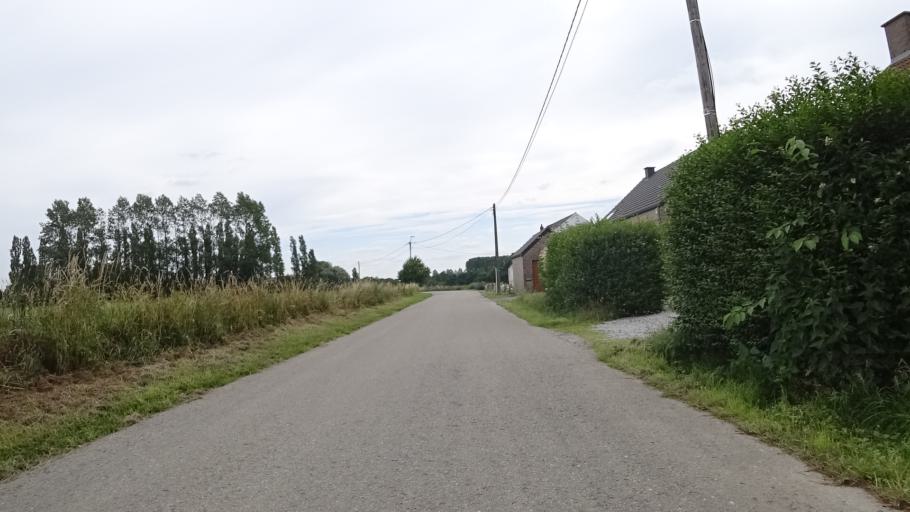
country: BE
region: Wallonia
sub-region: Province du Brabant Wallon
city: Louvain-la-Neuve
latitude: 50.6668
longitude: 4.6465
